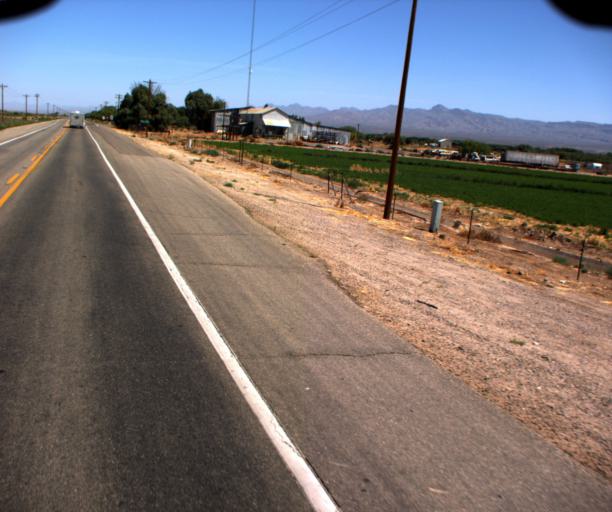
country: US
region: Arizona
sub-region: Graham County
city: Pima
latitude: 32.9595
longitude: -109.9188
